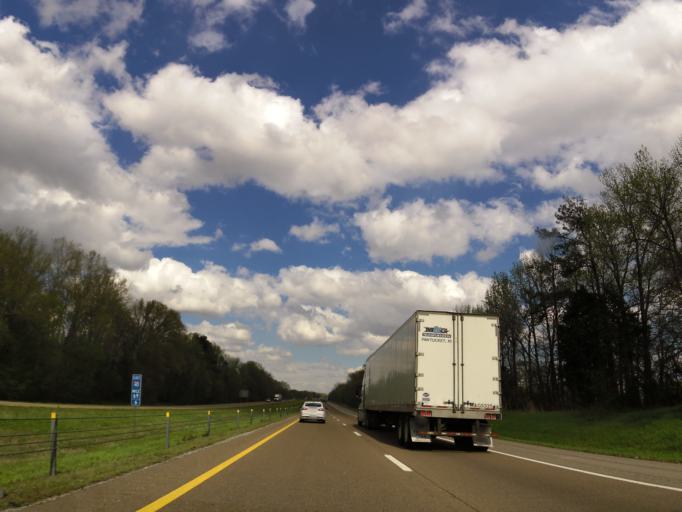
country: US
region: Tennessee
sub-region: Crockett County
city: Bells
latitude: 35.6057
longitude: -89.0324
